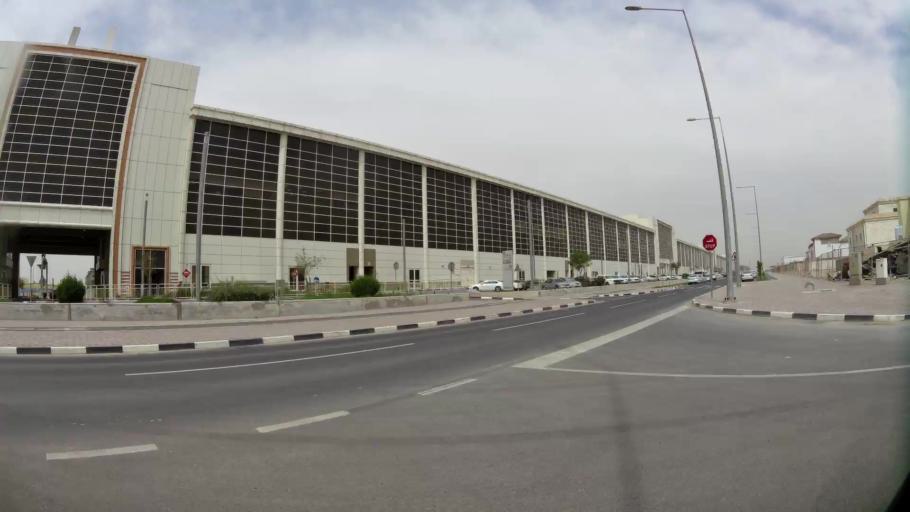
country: QA
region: Baladiyat ar Rayyan
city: Ar Rayyan
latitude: 25.1998
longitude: 51.4516
